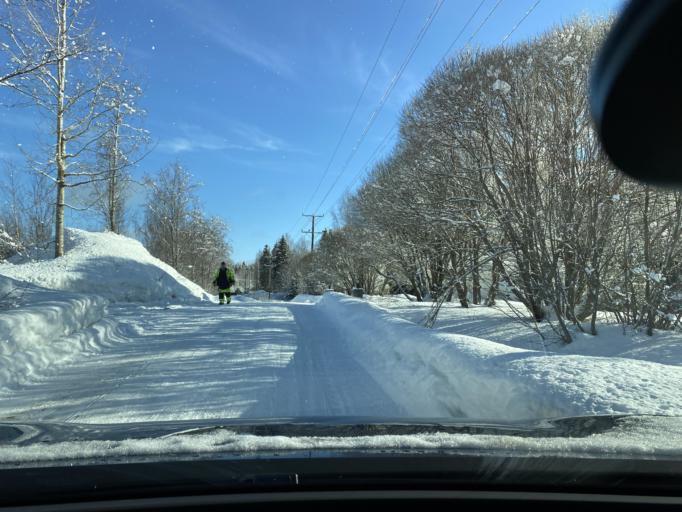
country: FI
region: Southern Savonia
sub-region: Mikkeli
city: Kangasniemi
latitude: 62.0155
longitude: 26.6097
